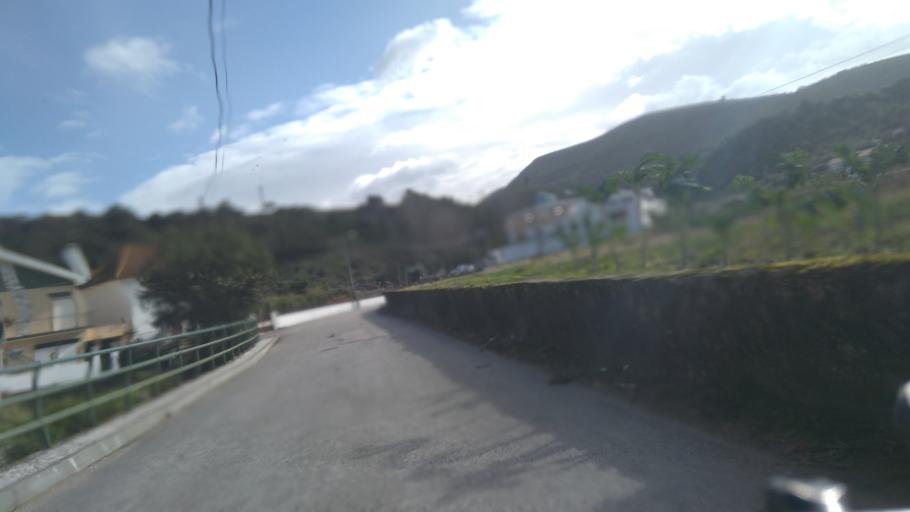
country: PT
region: Leiria
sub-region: Porto de Mos
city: Porto de Mos
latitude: 39.5856
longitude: -8.8207
